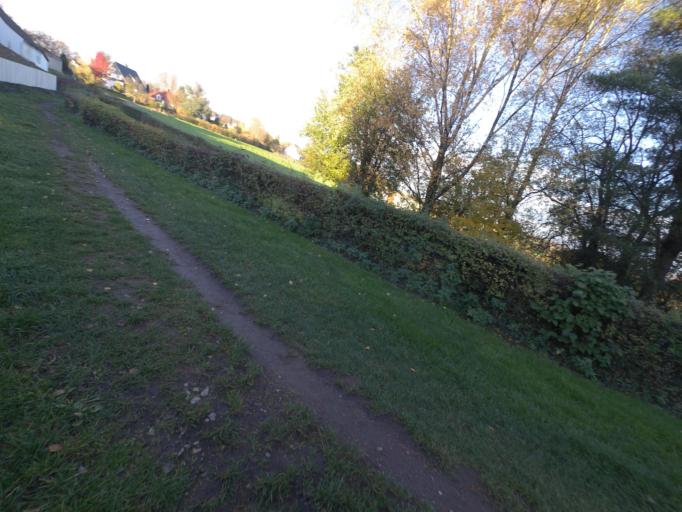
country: DE
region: North Rhine-Westphalia
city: Sprockhovel
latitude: 51.3375
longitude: 7.2880
